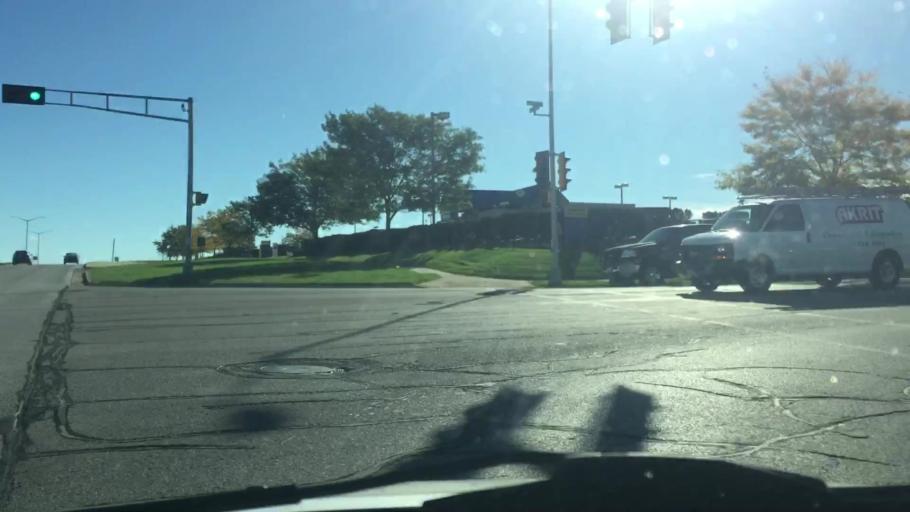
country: US
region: Wisconsin
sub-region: Waukesha County
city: Waukesha
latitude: 43.0363
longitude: -88.1794
